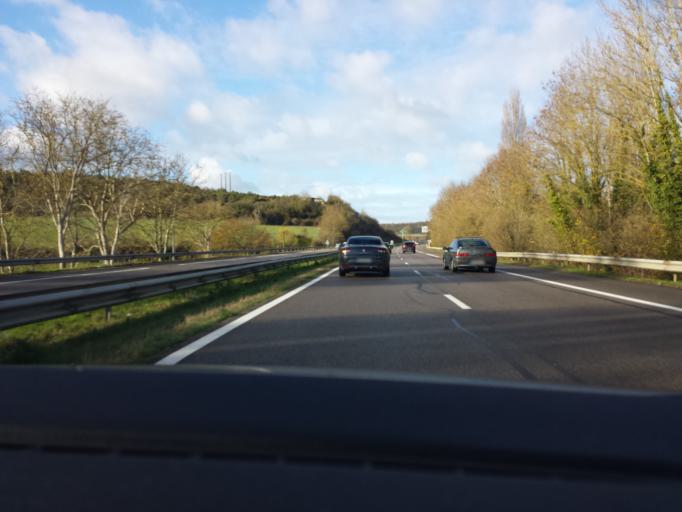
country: FR
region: Haute-Normandie
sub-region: Departement de l'Eure
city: Pacy-sur-Eure
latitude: 49.0087
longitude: 1.3638
